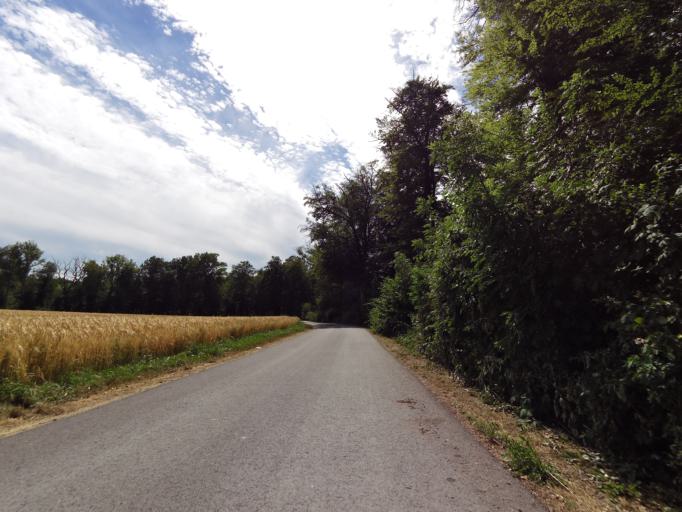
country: CH
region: Aargau
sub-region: Bezirk Rheinfelden
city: Mohlin
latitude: 47.5800
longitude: 7.8397
